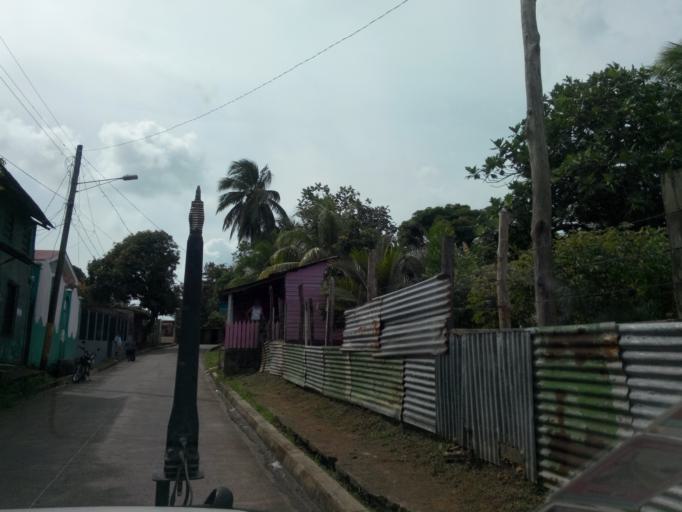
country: NI
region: Atlantico Sur
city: Bluefields
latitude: 12.0003
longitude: -83.7658
